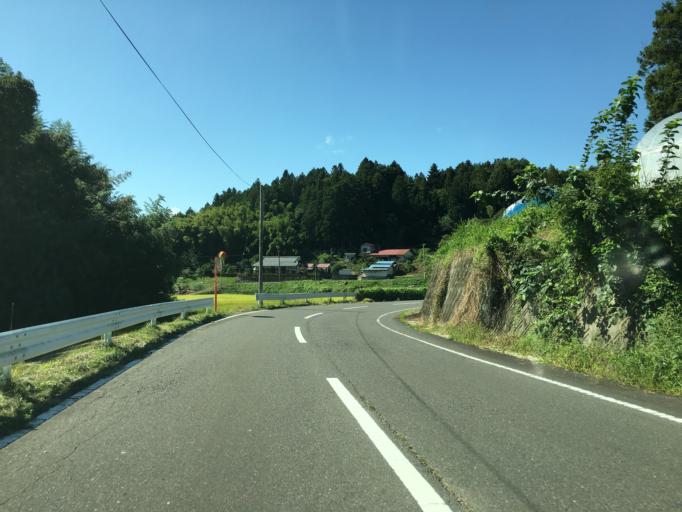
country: JP
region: Fukushima
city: Sukagawa
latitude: 37.2794
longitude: 140.4617
